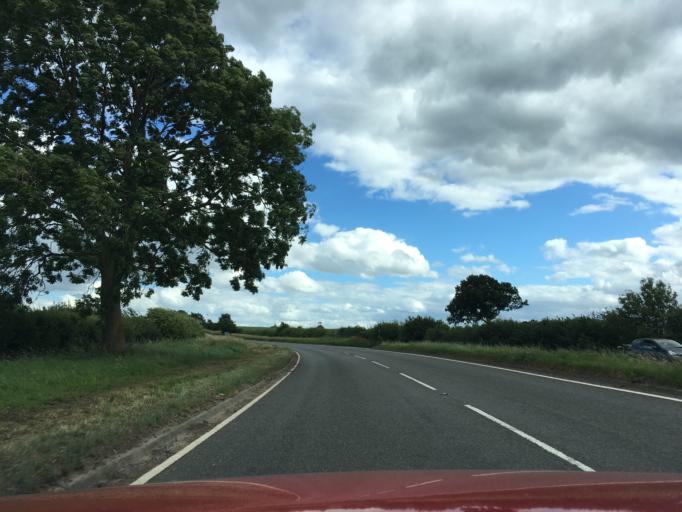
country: GB
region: England
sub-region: Leicestershire
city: Market Bosworth
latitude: 52.6227
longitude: -1.4819
